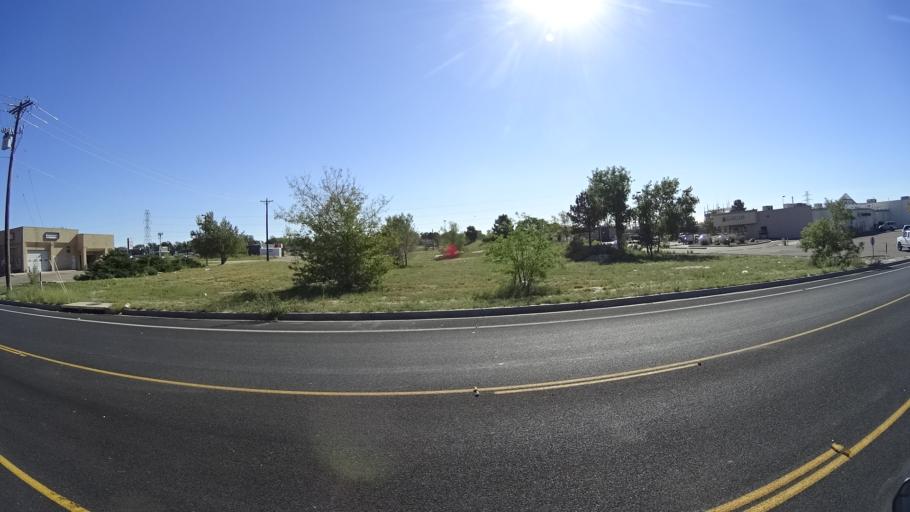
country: US
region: Colorado
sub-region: El Paso County
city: Stratmoor
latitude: 38.7941
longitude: -104.7597
